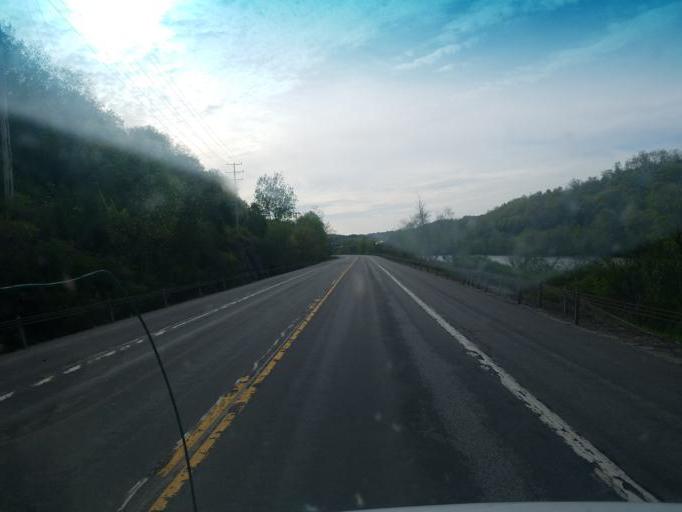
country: US
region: New York
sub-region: Herkimer County
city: Little Falls
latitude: 43.0341
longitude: -74.8329
